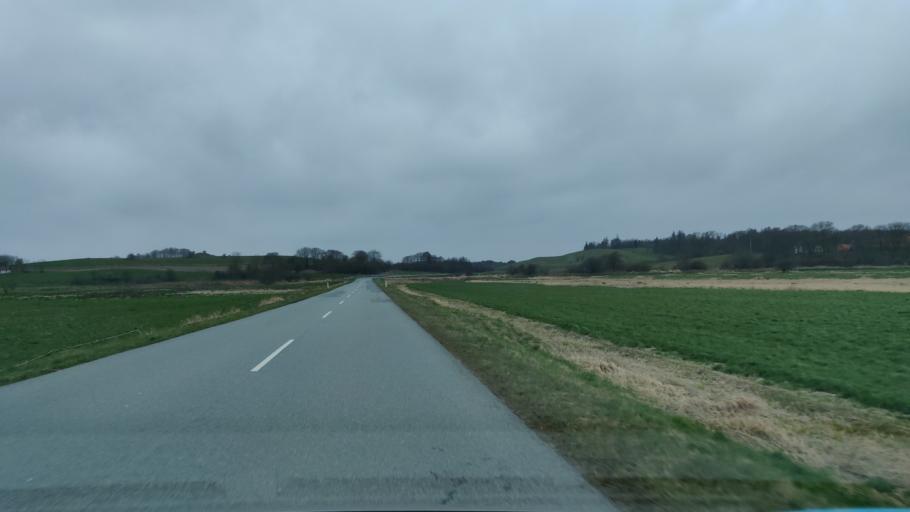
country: DK
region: Central Jutland
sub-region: Skive Kommune
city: Hojslev
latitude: 56.5700
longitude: 9.2442
